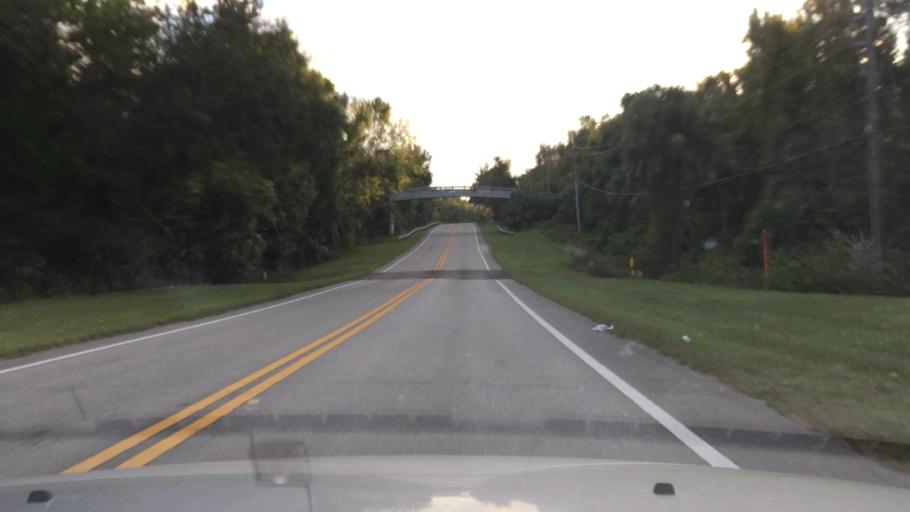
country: US
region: Florida
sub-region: Volusia County
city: Ormond Beach
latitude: 29.2962
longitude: -81.1071
